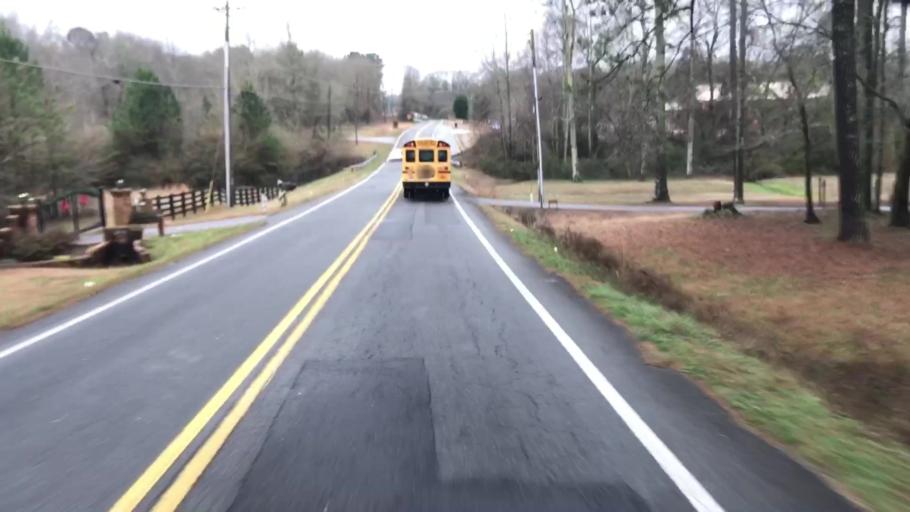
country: US
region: Georgia
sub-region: Walton County
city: Loganville
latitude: 33.8035
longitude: -83.9671
